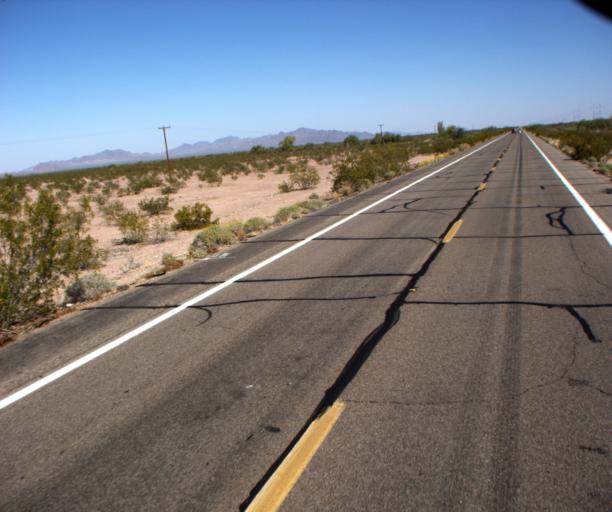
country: US
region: Arizona
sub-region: La Paz County
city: Quartzsite
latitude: 33.3472
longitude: -114.2170
